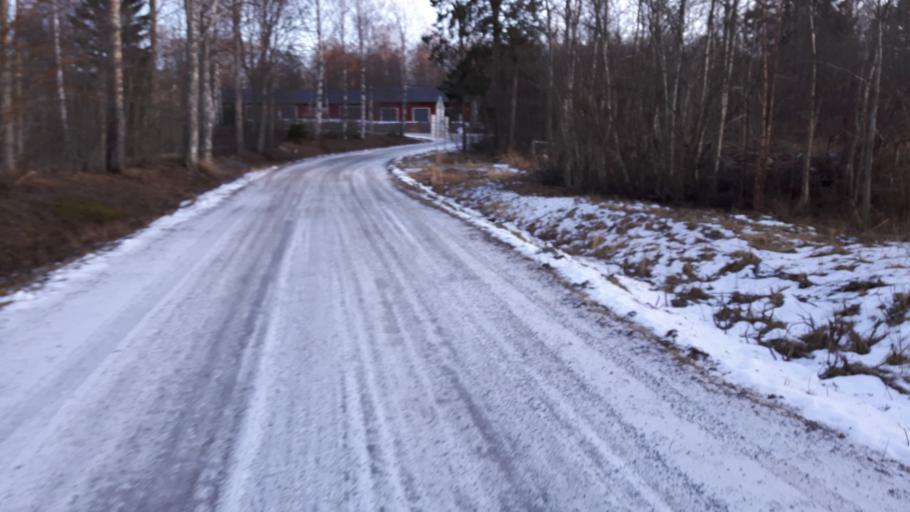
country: SE
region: Vaesternorrland
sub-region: Haernoesands Kommun
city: Haernoesand
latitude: 62.6200
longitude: 17.9371
